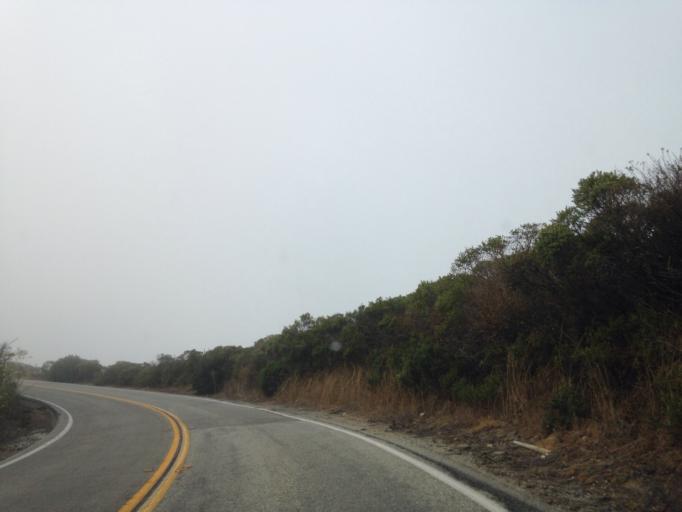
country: US
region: California
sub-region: San Mateo County
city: Highlands-Baywood Park
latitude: 37.4887
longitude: -122.3636
